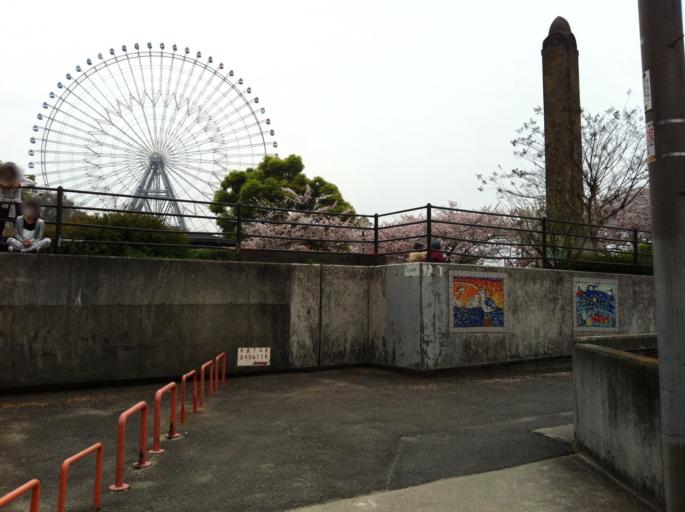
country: JP
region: Hyogo
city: Amagasaki
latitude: 34.6581
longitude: 135.4329
